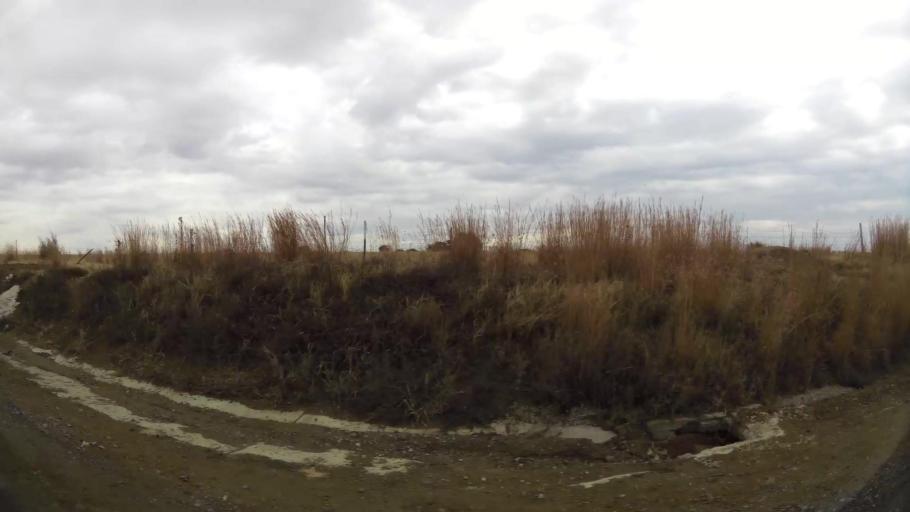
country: ZA
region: Orange Free State
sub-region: Fezile Dabi District Municipality
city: Kroonstad
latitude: -27.6224
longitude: 27.2428
